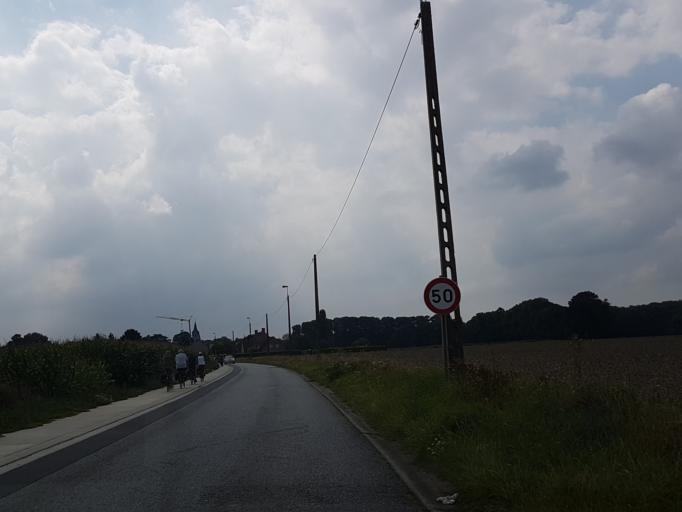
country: BE
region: Flanders
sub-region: Provincie Vlaams-Brabant
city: Kortenberg
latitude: 50.8821
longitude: 4.5785
